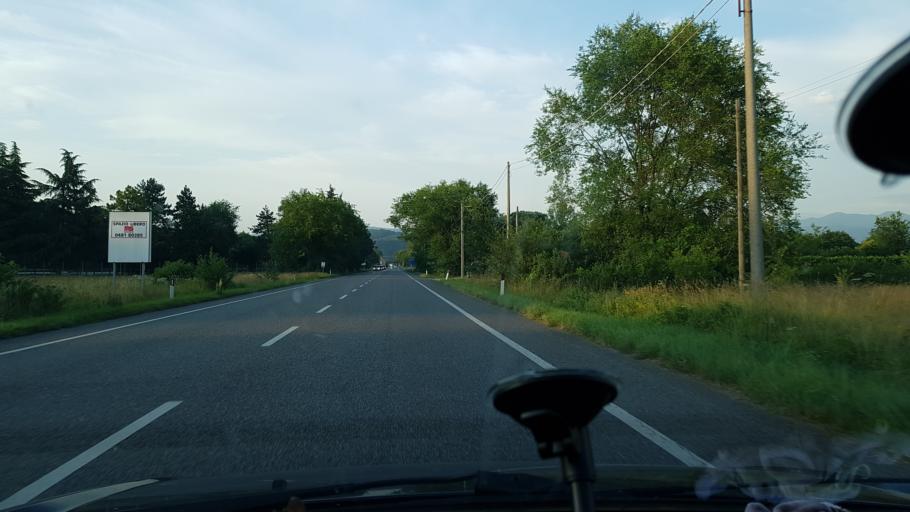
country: IT
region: Friuli Venezia Giulia
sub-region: Provincia di Gorizia
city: Savogna d'Isonzo
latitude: 45.9181
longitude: 13.5635
